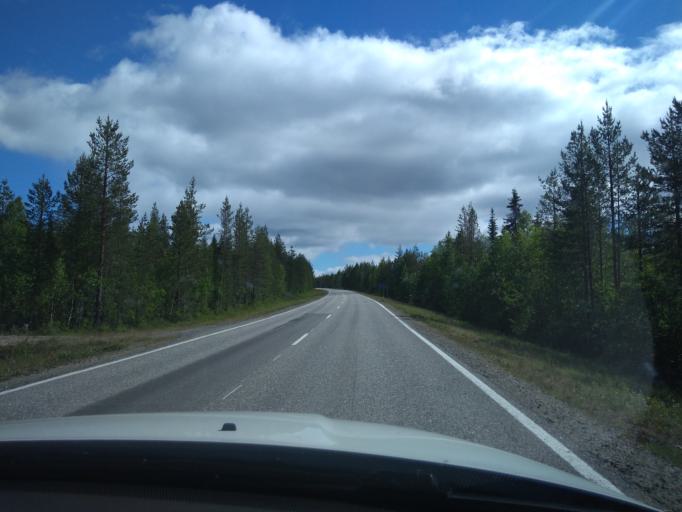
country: FI
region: Lapland
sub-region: Tunturi-Lappi
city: Kittilae
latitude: 67.2580
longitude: 24.8943
